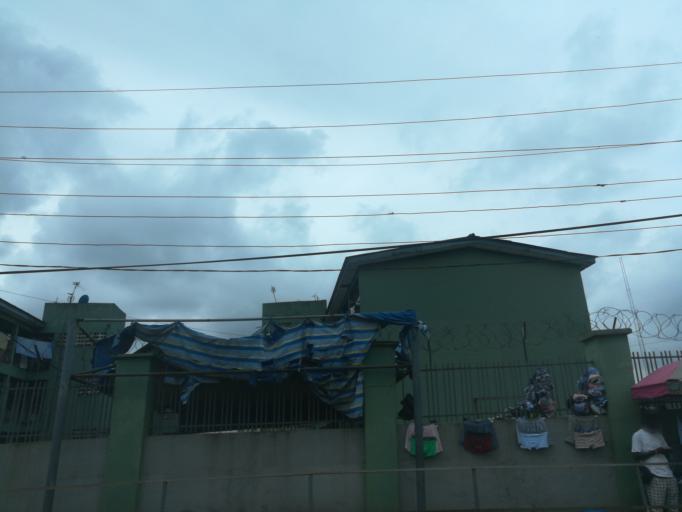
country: NG
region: Lagos
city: Ikeja
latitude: 6.5959
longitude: 3.3373
